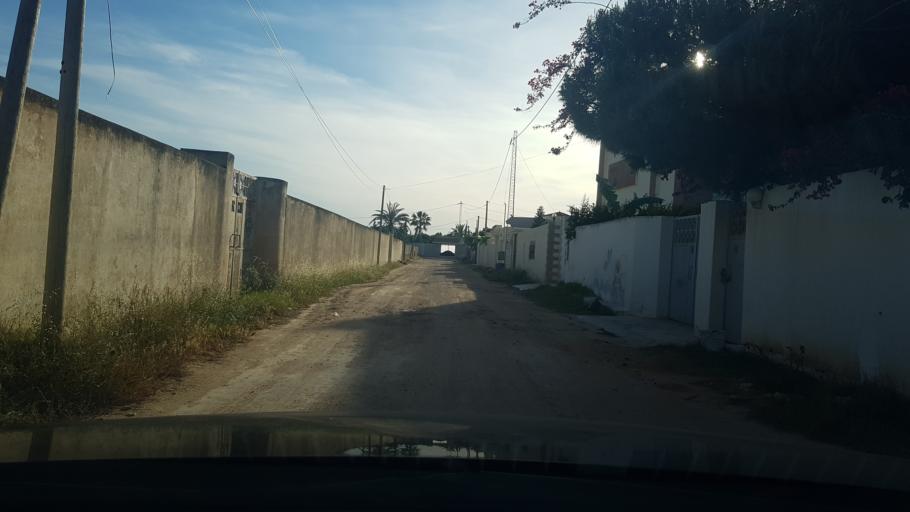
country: TN
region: Safaqis
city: Al Qarmadah
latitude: 34.8308
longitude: 10.7630
